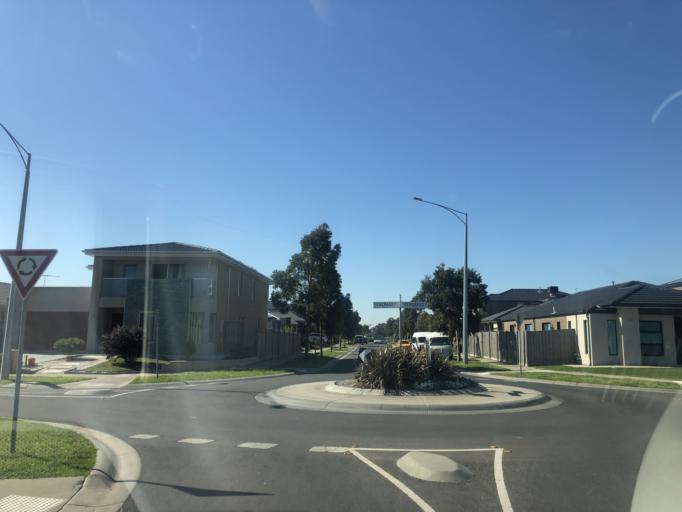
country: AU
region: Victoria
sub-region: Wyndham
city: Hoppers Crossing
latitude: -37.9089
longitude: 144.7173
